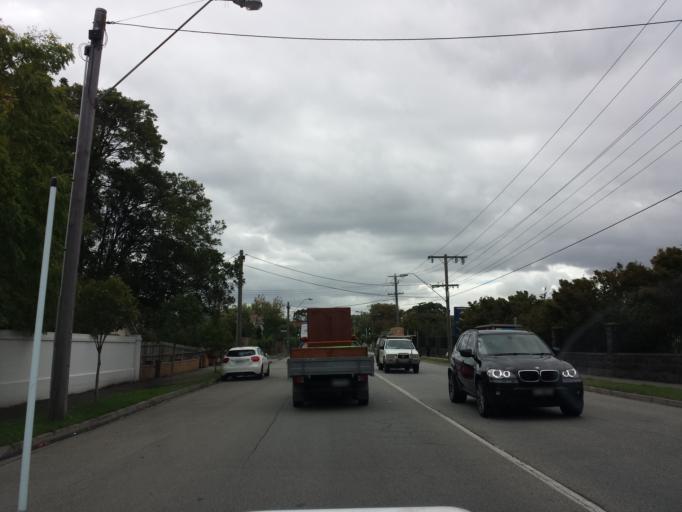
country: AU
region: Victoria
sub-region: Stonnington
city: Glen Iris
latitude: -37.8620
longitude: 145.0508
